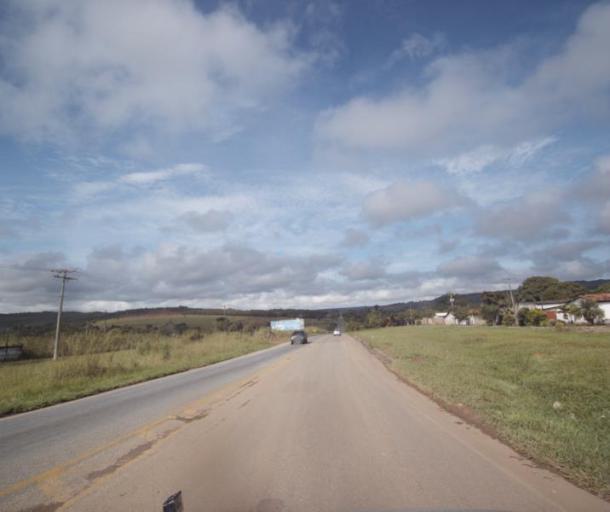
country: BR
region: Goias
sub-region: Pirenopolis
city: Pirenopolis
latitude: -15.7914
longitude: -48.7732
